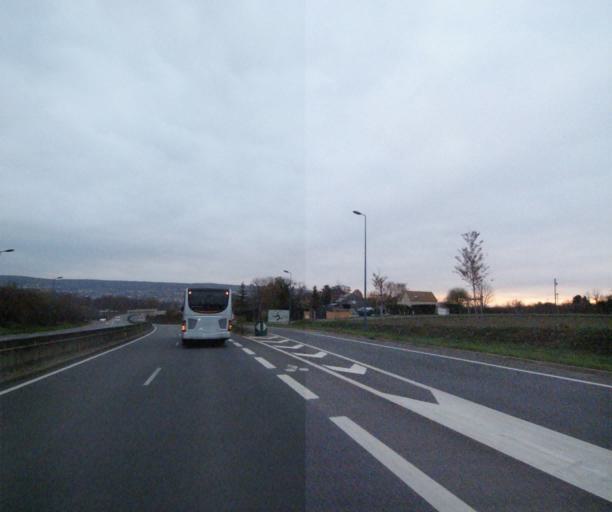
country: FR
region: Ile-de-France
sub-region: Departement des Yvelines
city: Medan
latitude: 48.9631
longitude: 1.9886
